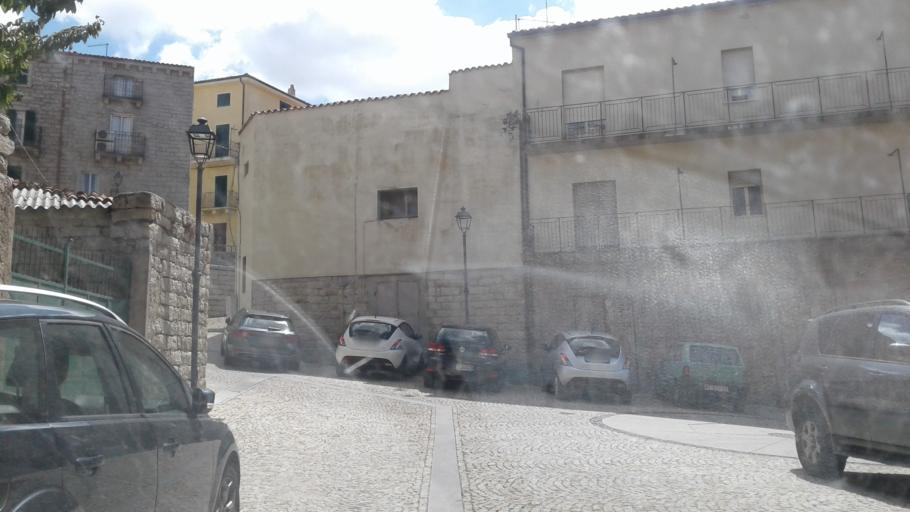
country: IT
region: Sardinia
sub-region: Provincia di Olbia-Tempio
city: Calangianus
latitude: 40.9212
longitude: 9.1935
